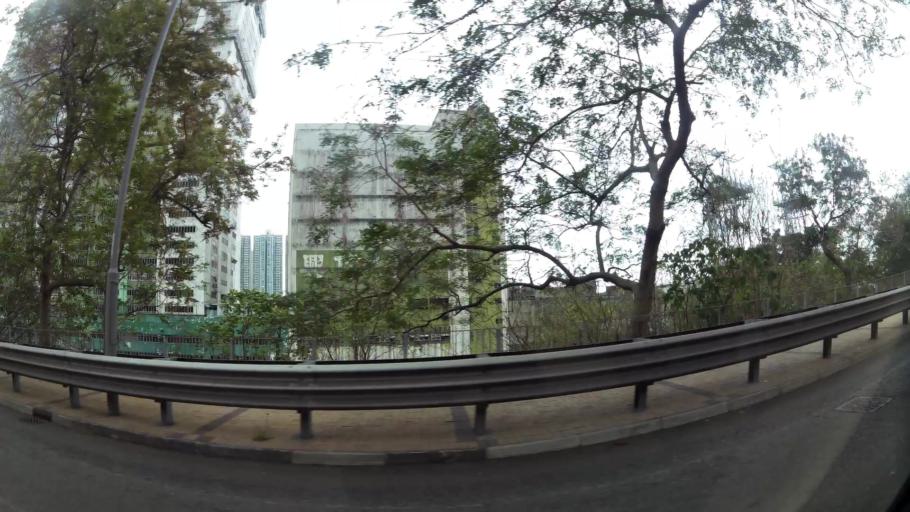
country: HK
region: Central and Western
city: Central
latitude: 22.2493
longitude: 114.1454
